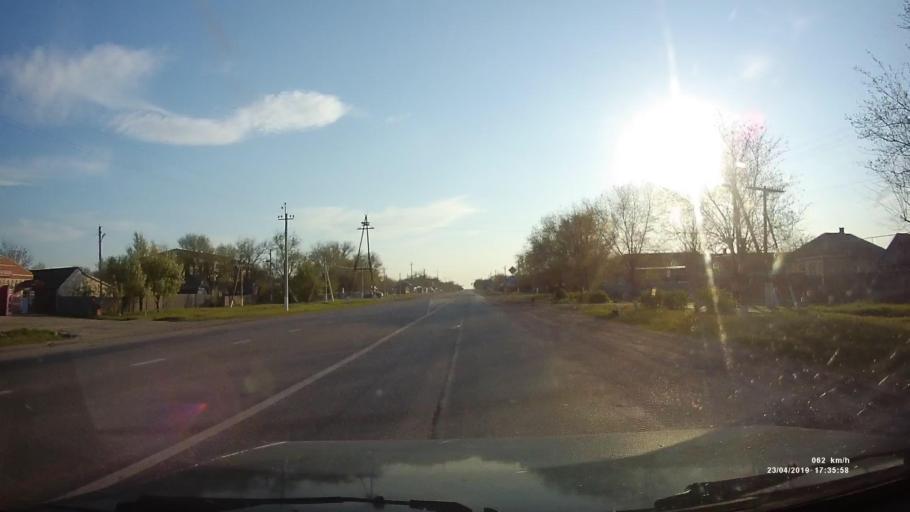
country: RU
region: Kalmykiya
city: Priyutnoye
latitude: 46.0979
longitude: 43.5124
